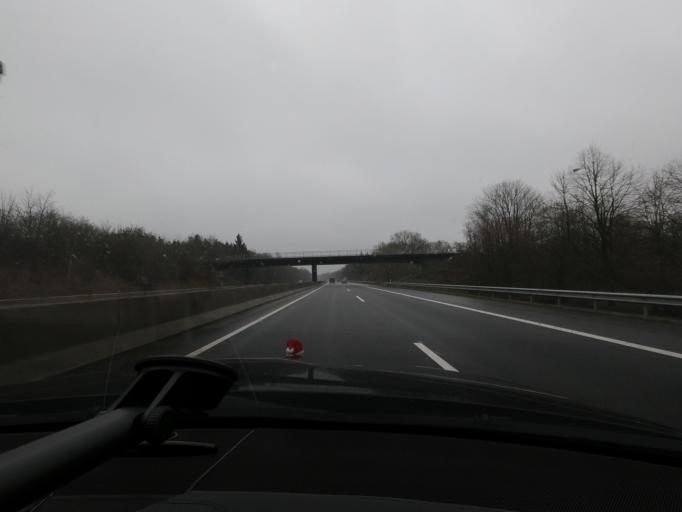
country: DE
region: Schleswig-Holstein
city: Bokel
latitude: 54.2378
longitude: 9.8245
